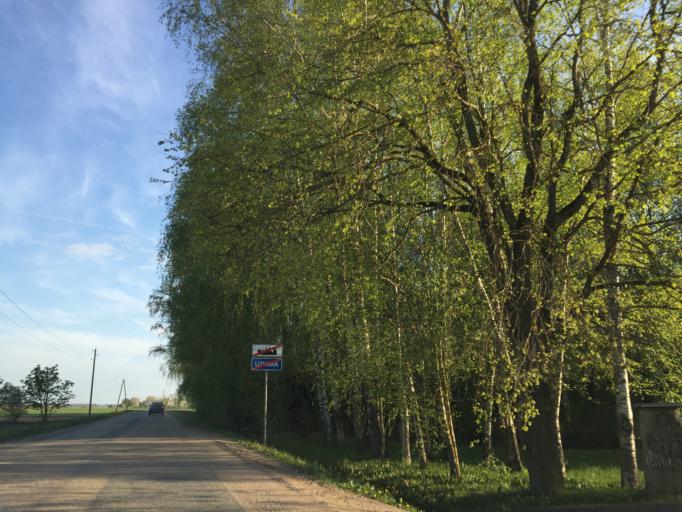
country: LV
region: Bauskas Rajons
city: Bauska
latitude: 56.3038
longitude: 24.2613
